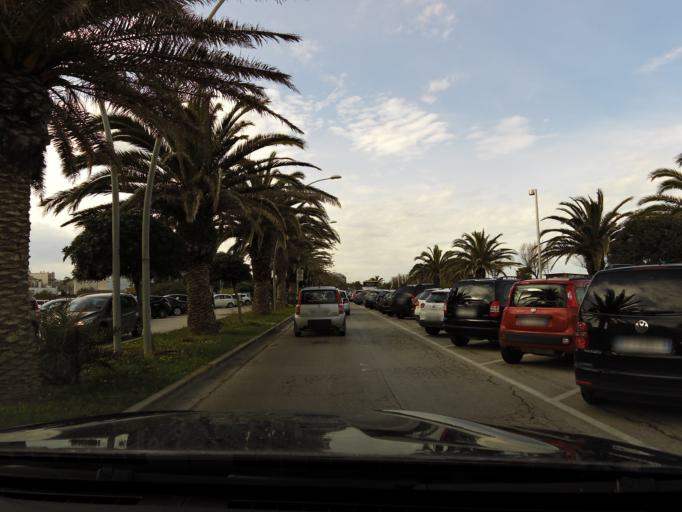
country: IT
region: The Marches
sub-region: Provincia di Macerata
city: Portocivitanova
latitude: 43.3028
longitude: 13.7368
